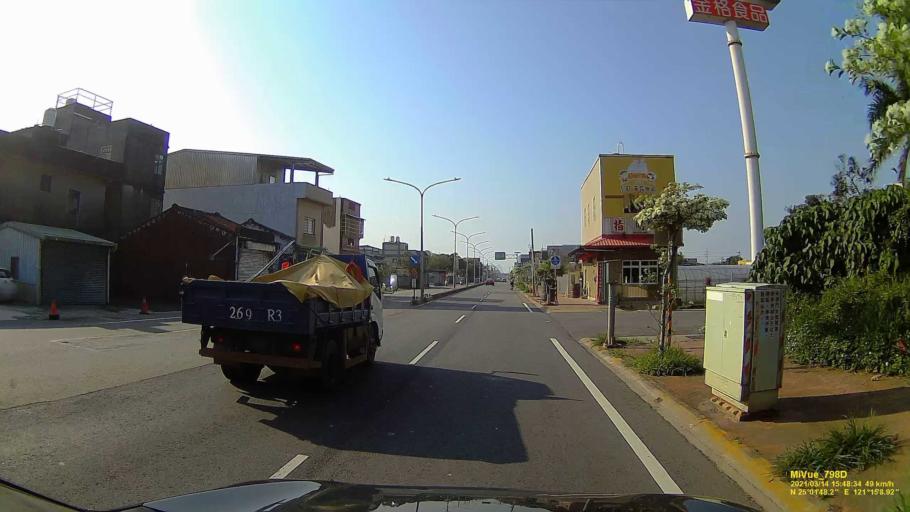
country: TW
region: Taiwan
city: Taoyuan City
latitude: 25.0303
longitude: 121.2522
